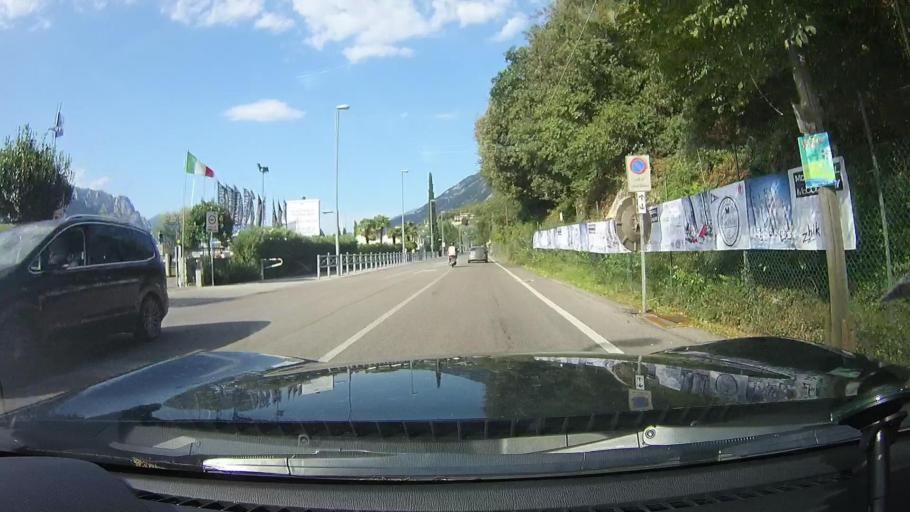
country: IT
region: Veneto
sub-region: Provincia di Verona
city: Malcesine
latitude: 45.7952
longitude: 10.8352
